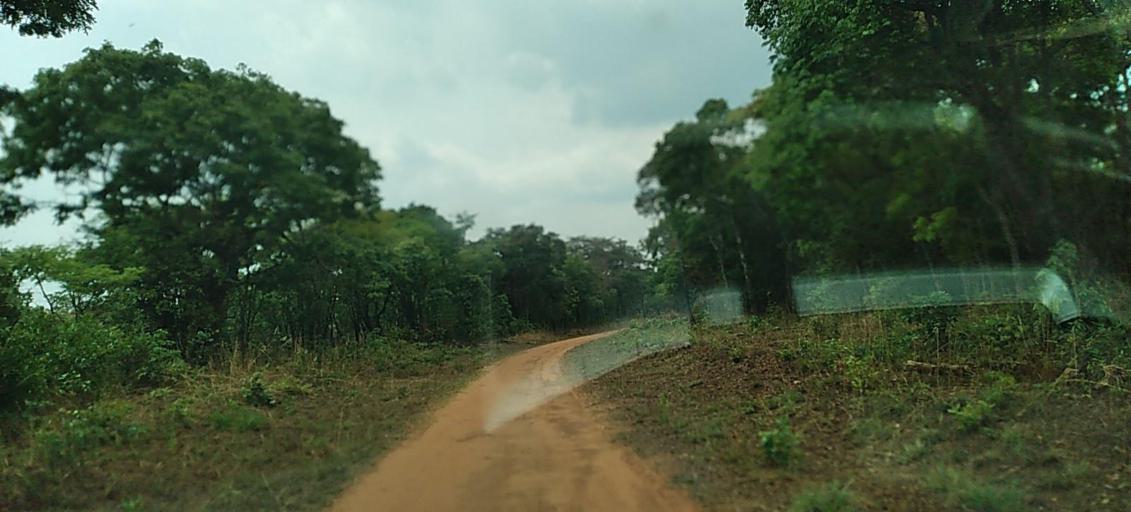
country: ZM
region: North-Western
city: Mwinilunga
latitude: -11.5522
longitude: 24.7736
